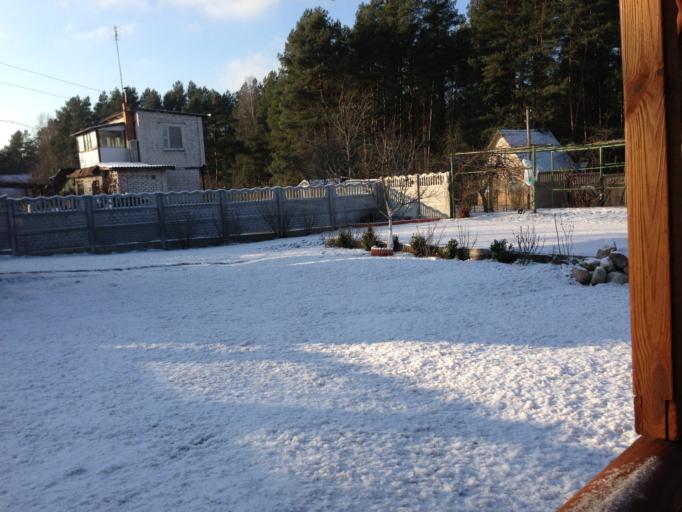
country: LT
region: Alytaus apskritis
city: Druskininkai
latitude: 53.9212
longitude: 24.1898
